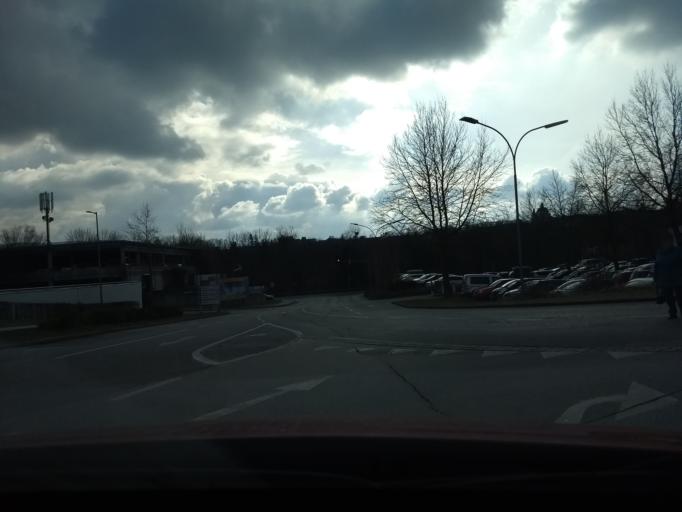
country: AT
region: Upper Austria
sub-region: Politischer Bezirk Steyr-Land
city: Garsten
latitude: 48.0443
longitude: 14.3903
